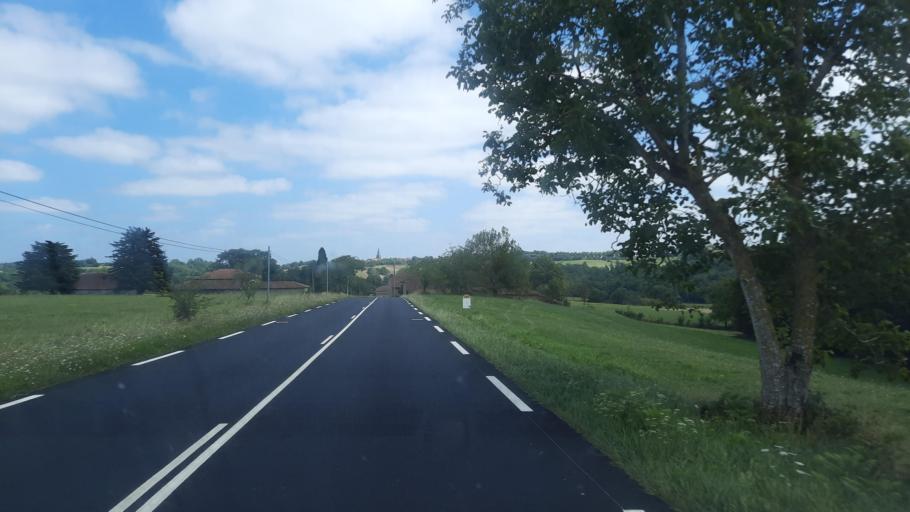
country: FR
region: Midi-Pyrenees
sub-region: Departement de la Haute-Garonne
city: Boulogne-sur-Gesse
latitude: 43.2964
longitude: 0.6196
